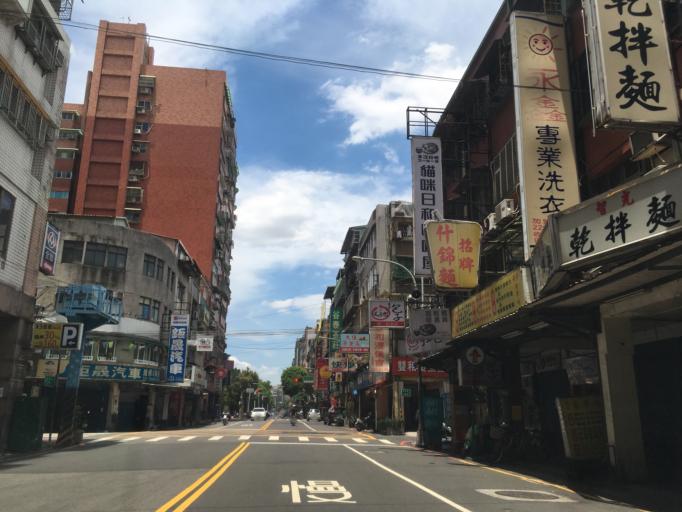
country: TW
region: Taipei
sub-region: Taipei
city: Banqiao
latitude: 24.9976
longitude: 121.5120
